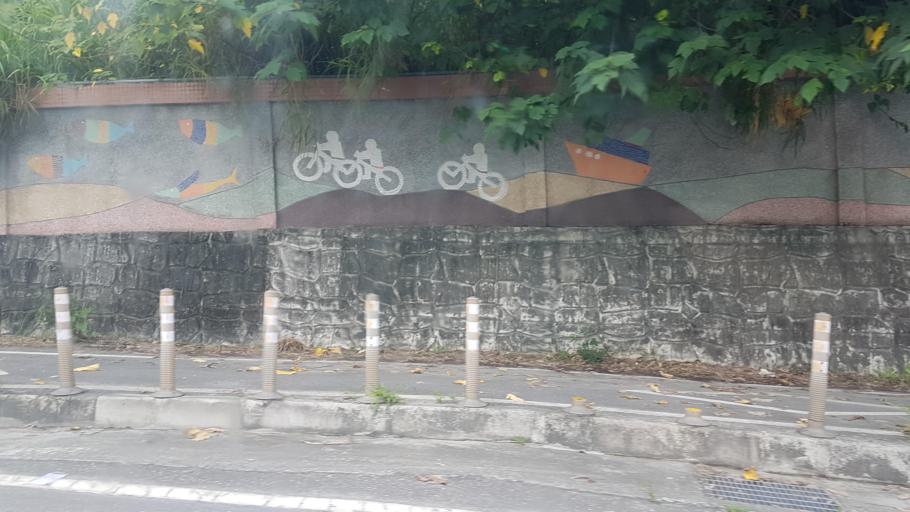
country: TW
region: Taiwan
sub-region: Hualien
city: Hualian
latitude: 24.0070
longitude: 121.6377
